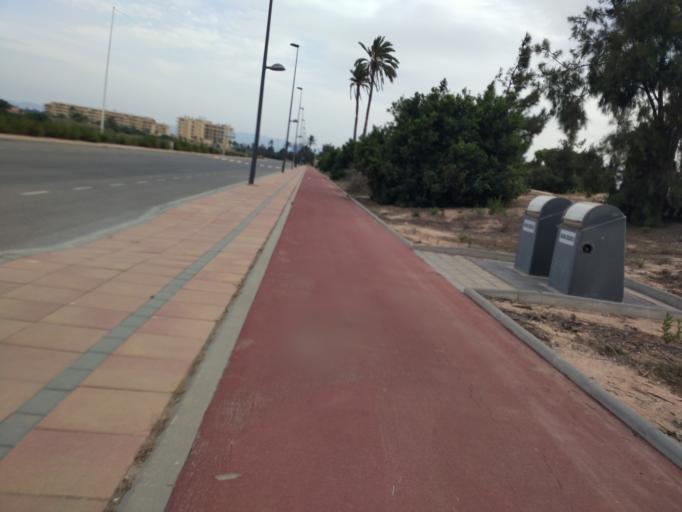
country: ES
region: Murcia
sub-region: Murcia
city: Los Alcazares
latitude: 37.7342
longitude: -0.8715
